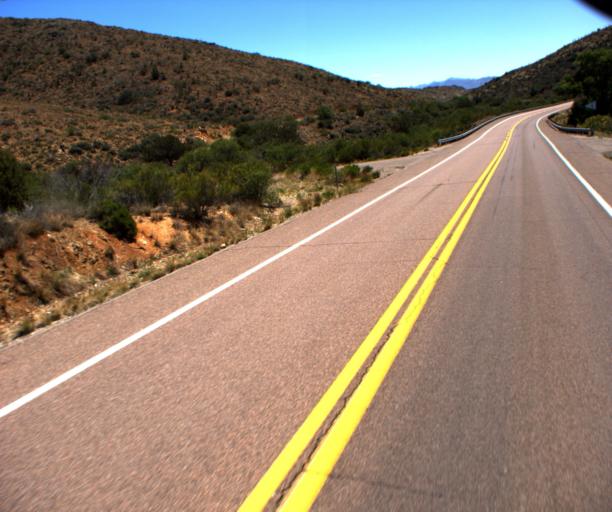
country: US
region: Arizona
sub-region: Yavapai County
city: Bagdad
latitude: 34.5610
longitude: -113.1654
